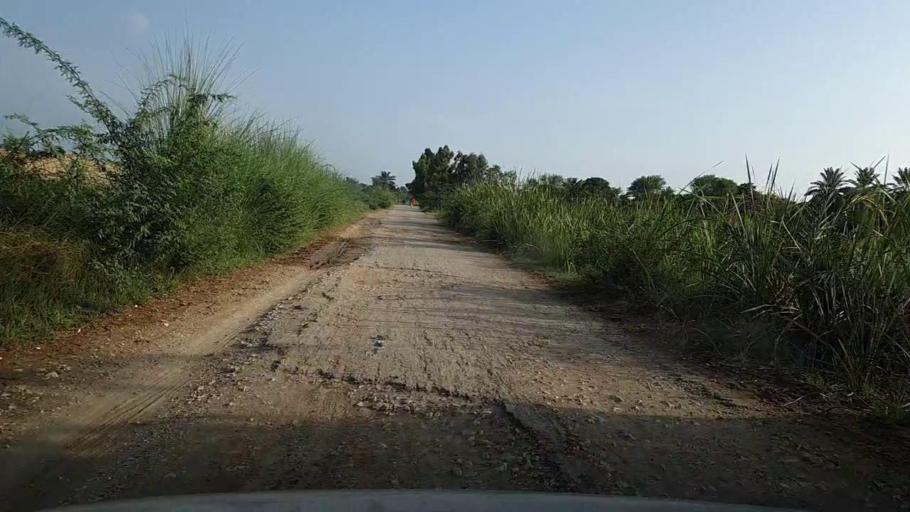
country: PK
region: Sindh
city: Pad Idan
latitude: 26.8059
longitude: 68.2359
